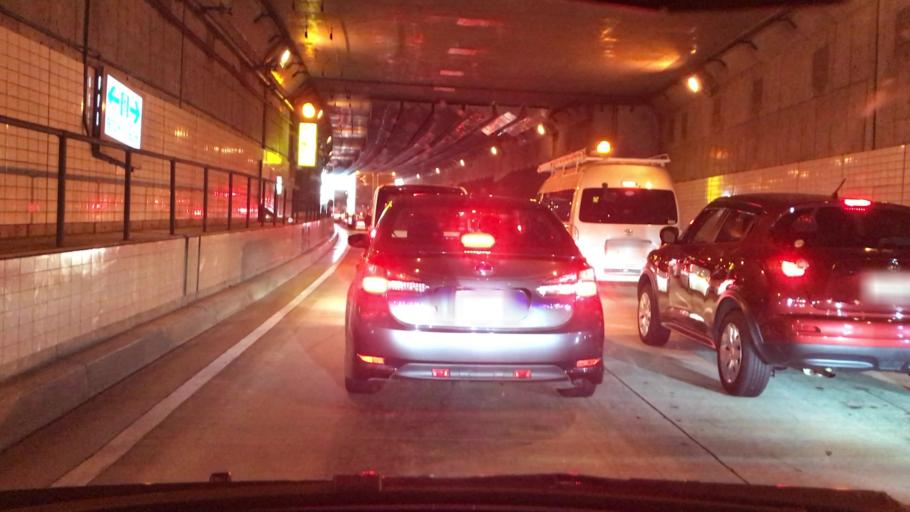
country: JP
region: Hyogo
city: Kobe
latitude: 34.7045
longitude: 135.2009
